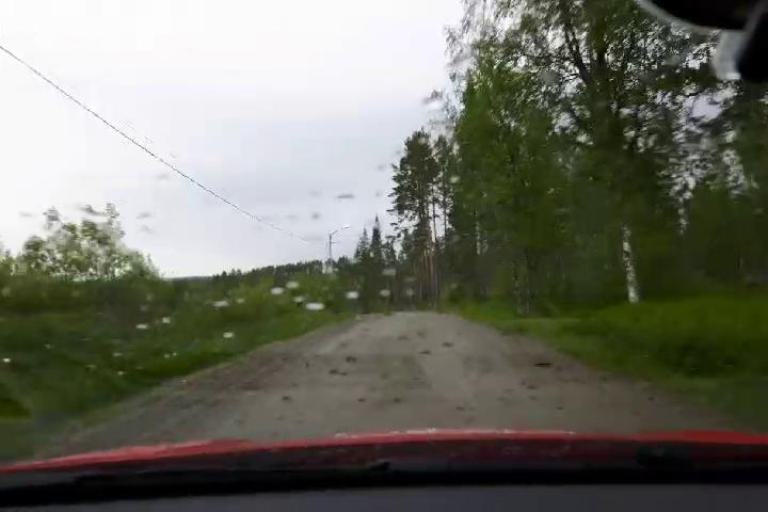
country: SE
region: Jaemtland
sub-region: Bergs Kommun
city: Hoverberg
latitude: 62.7455
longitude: 14.4540
